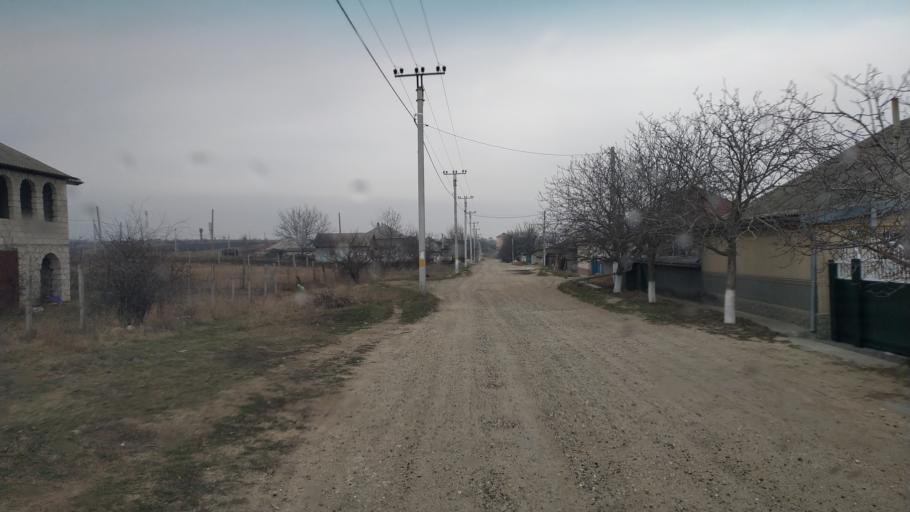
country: MD
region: Chisinau
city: Singera
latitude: 46.8278
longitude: 28.9644
